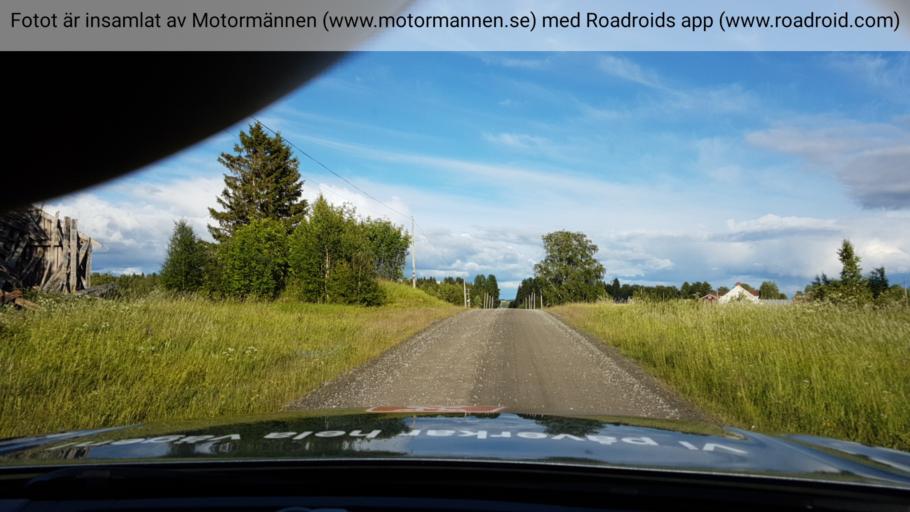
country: SE
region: Jaemtland
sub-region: Bergs Kommun
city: Hoverberg
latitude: 62.9347
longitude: 14.4243
